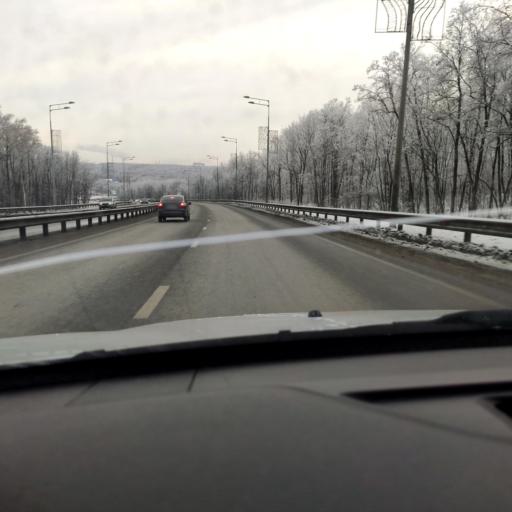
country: RU
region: Samara
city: Novosemeykino
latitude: 53.3141
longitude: 50.2305
